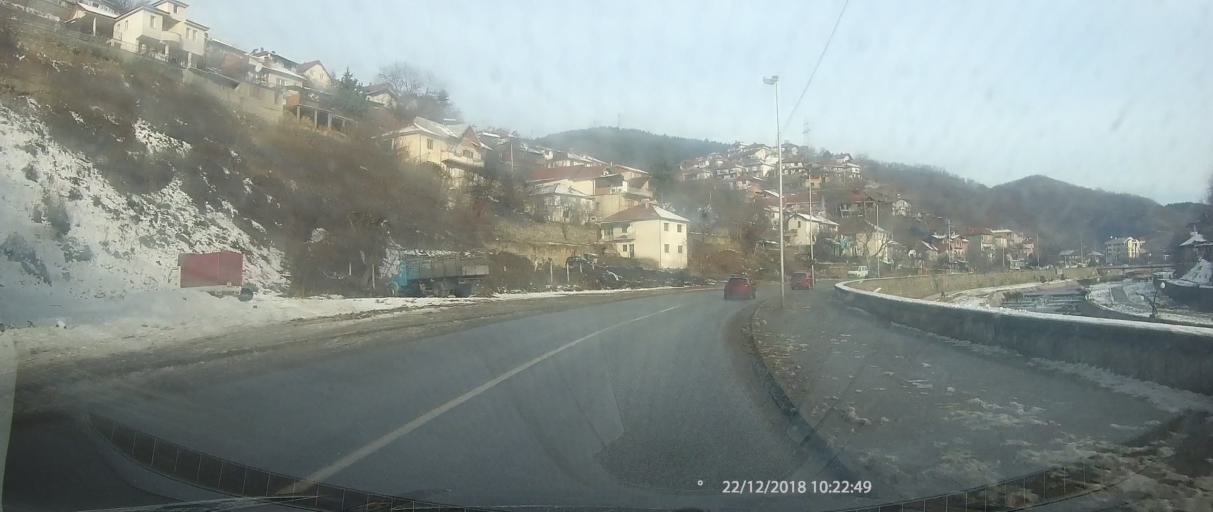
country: MK
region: Kriva Palanka
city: Kriva Palanka
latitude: 42.2043
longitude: 22.3332
